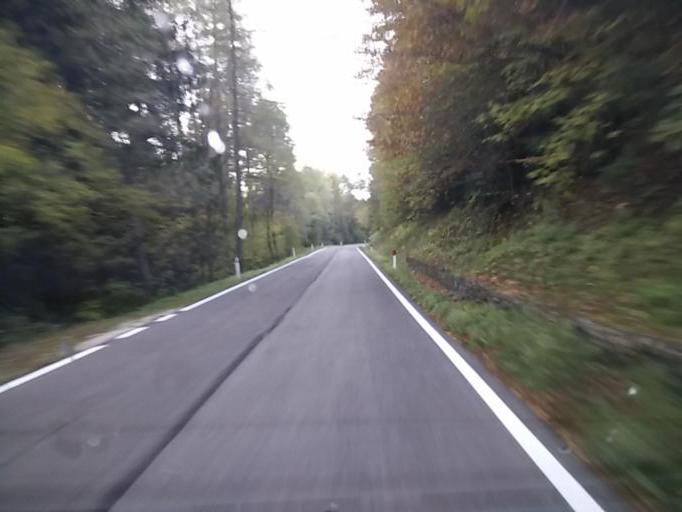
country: IT
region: Trentino-Alto Adige
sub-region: Provincia di Trento
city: Covelo
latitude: 45.9625
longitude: 11.0466
